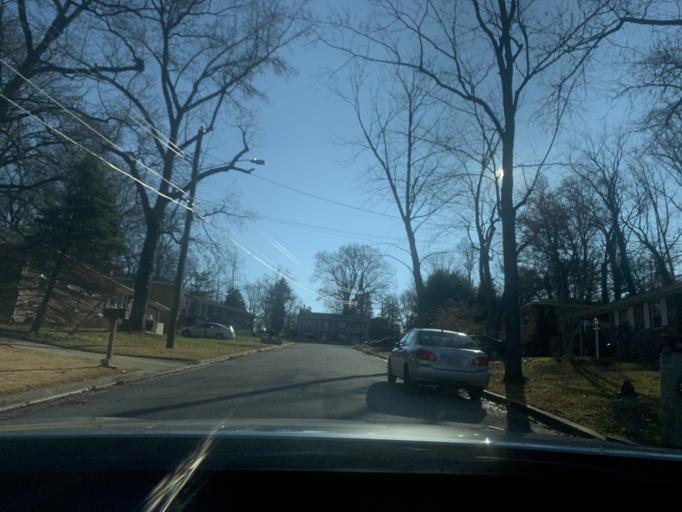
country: US
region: Maryland
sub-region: Prince George's County
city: Camp Springs
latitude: 38.8127
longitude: -76.9207
